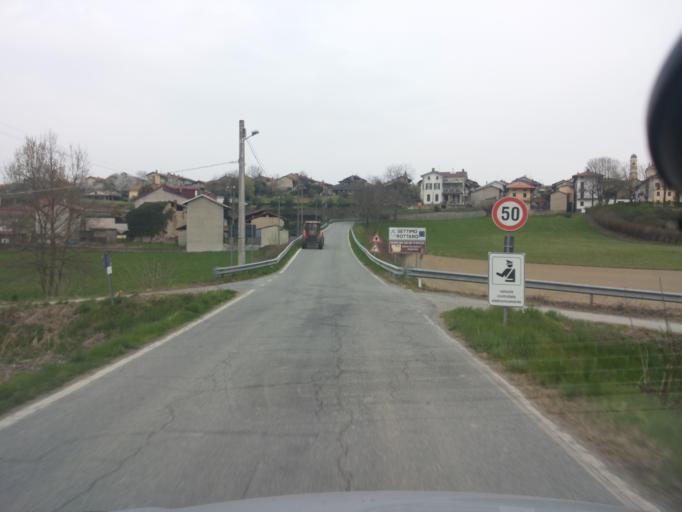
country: IT
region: Piedmont
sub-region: Provincia di Torino
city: Settimo Rottaro
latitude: 45.4056
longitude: 7.9880
